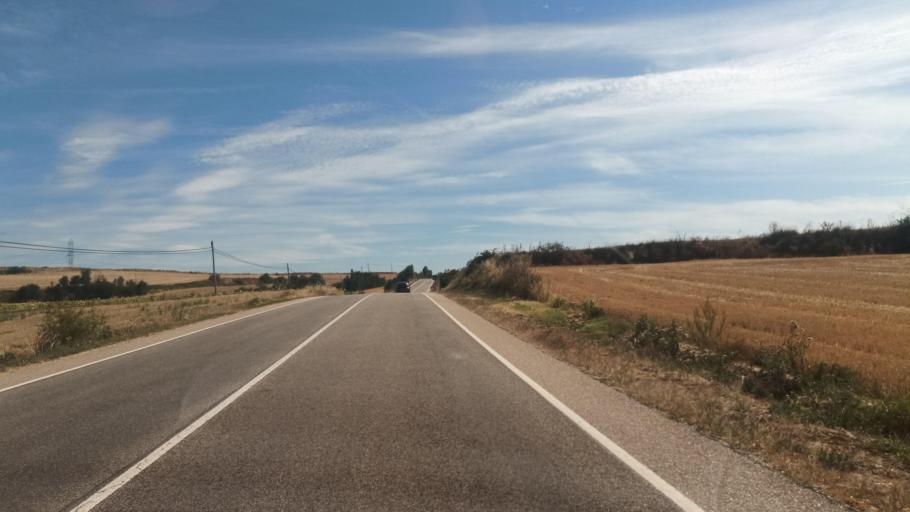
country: ES
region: Castille and Leon
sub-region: Provincia de Burgos
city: Aguilar de Bureba
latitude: 42.5765
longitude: -3.3333
